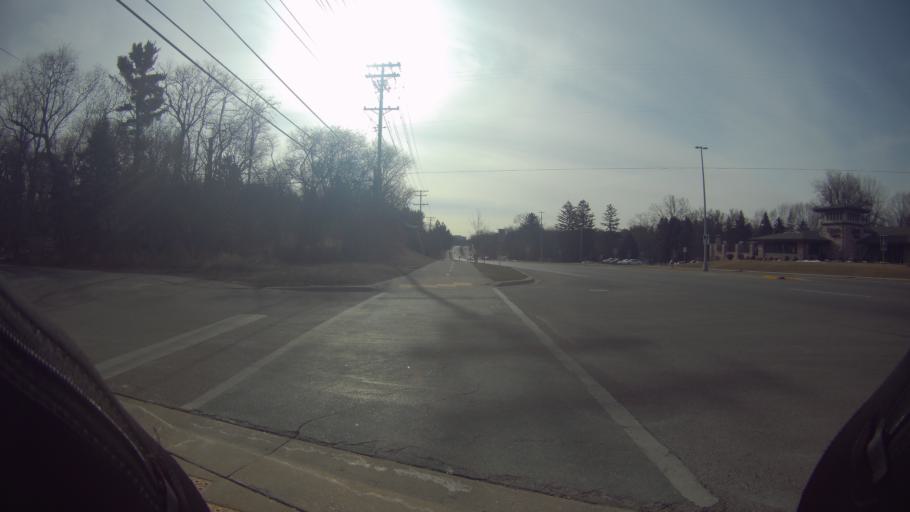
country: US
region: Wisconsin
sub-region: Dane County
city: Middleton
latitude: 43.0888
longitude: -89.4841
